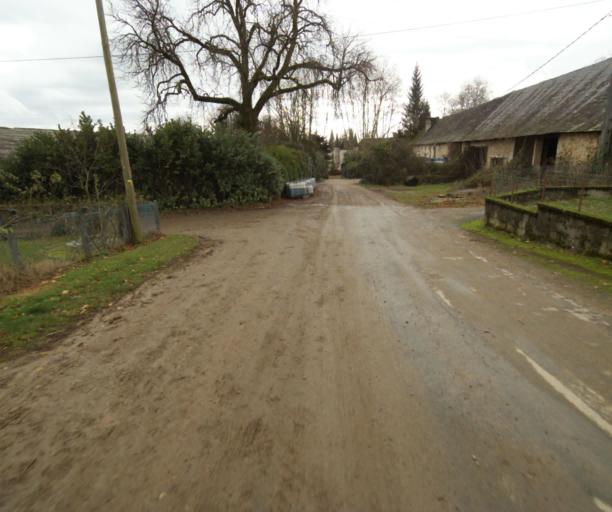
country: FR
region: Limousin
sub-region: Departement de la Correze
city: Saint-Mexant
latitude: 45.2726
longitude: 1.6181
